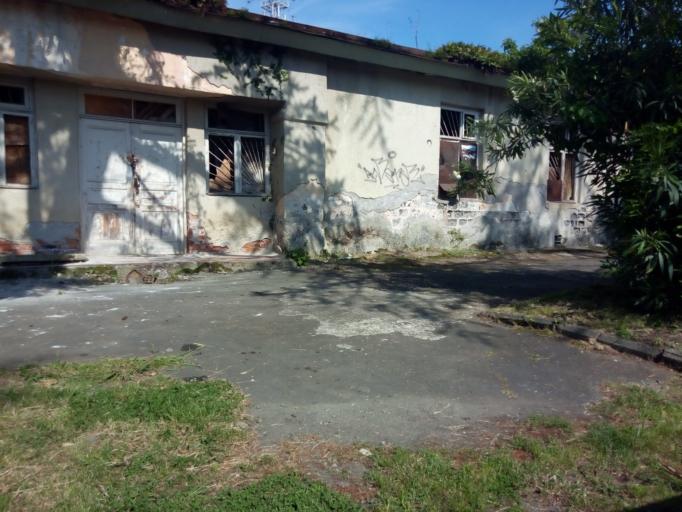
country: GE
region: Abkhazia
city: Sokhumi
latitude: 42.9971
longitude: 41.0199
